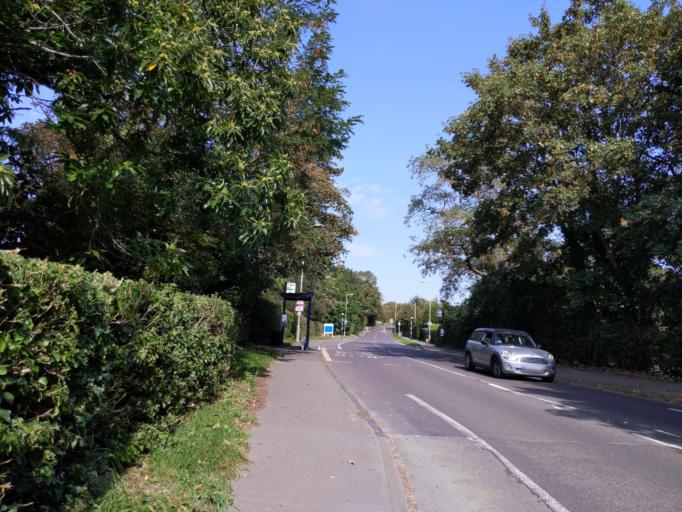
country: GB
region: England
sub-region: Oxfordshire
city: Cowley
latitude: 51.7178
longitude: -1.2281
